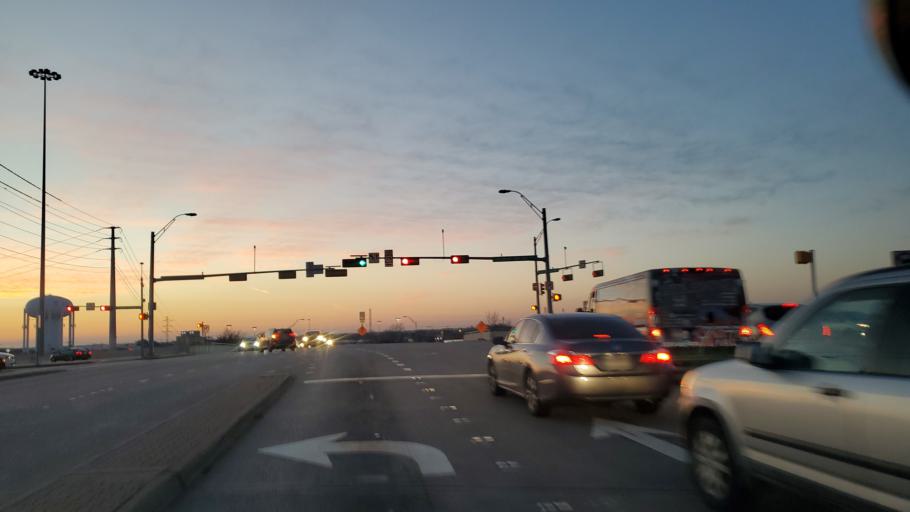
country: US
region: Texas
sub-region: Collin County
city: Plano
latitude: 33.0374
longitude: -96.7039
